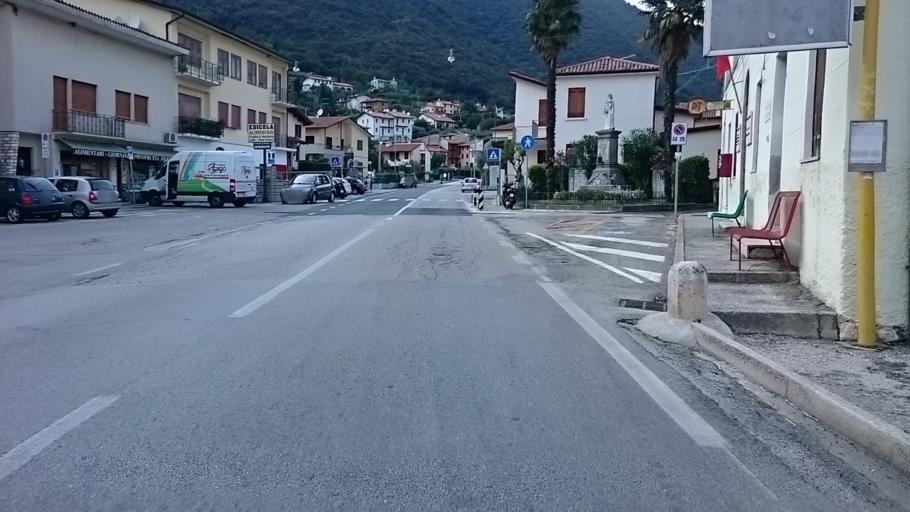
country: IT
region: Veneto
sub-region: Provincia di Vicenza
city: Campese
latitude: 45.8042
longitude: 11.7120
